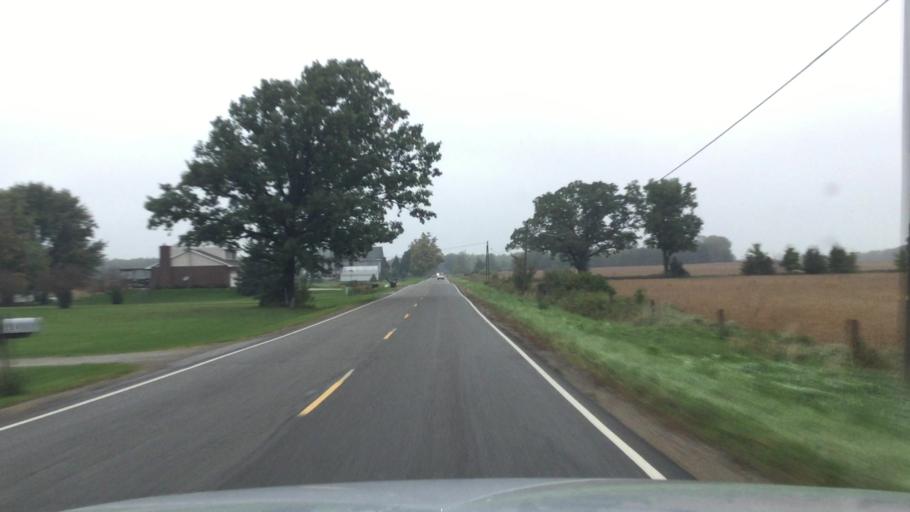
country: US
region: Michigan
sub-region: Shiawassee County
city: Corunna
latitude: 42.9219
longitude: -84.1241
